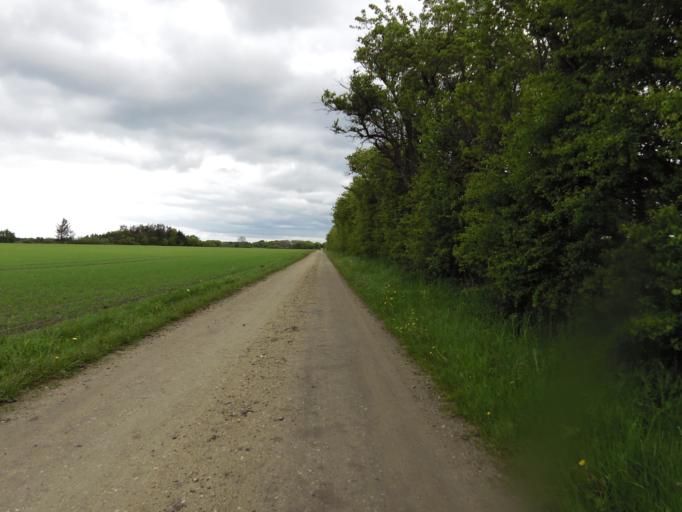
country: DK
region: South Denmark
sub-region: Haderslev Kommune
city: Gram
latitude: 55.2820
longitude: 9.0230
